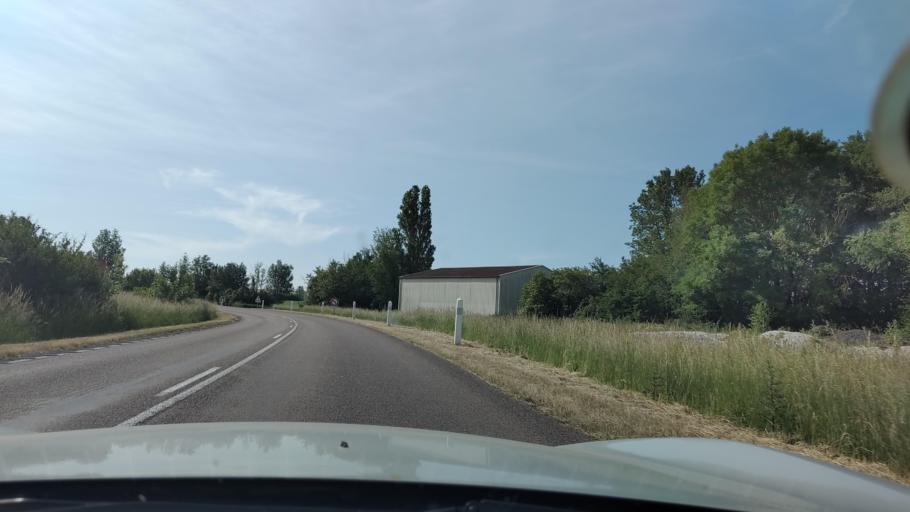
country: FR
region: Champagne-Ardenne
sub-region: Departement de l'Aube
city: Nogent-sur-Seine
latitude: 48.4678
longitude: 3.5659
